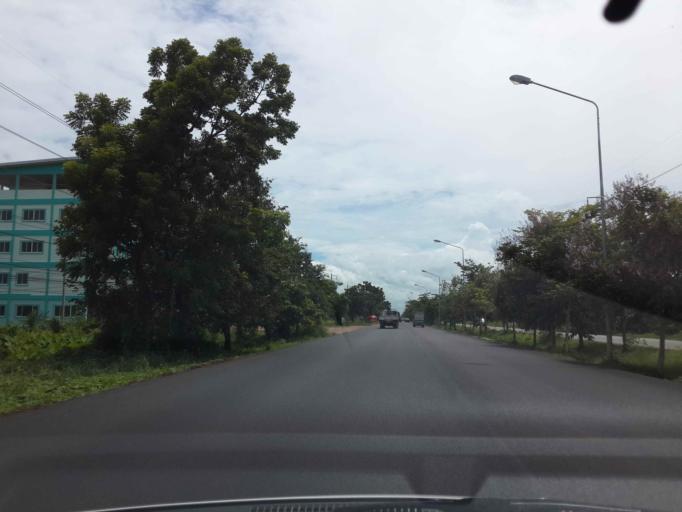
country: TH
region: Ratchaburi
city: Pak Tho
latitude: 13.4332
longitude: 99.8058
